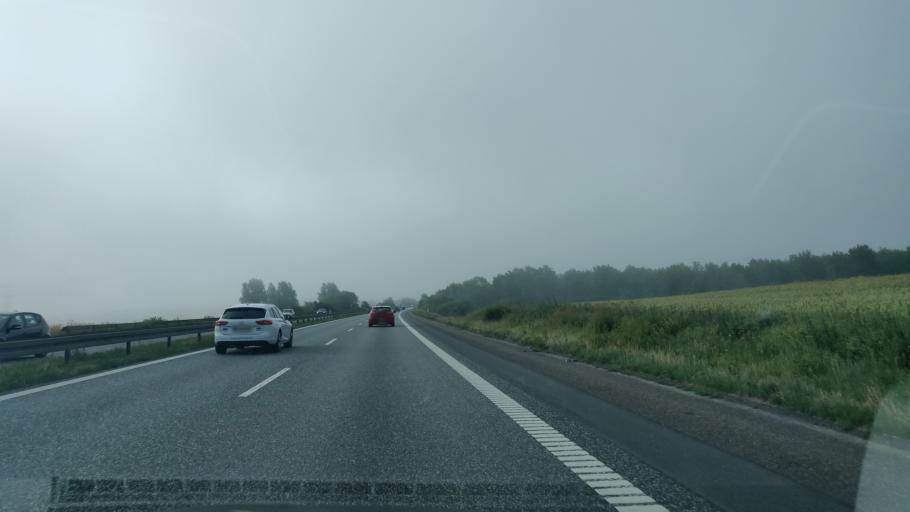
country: DK
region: Central Jutland
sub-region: Randers Kommune
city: Spentrup
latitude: 56.5133
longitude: 9.9665
